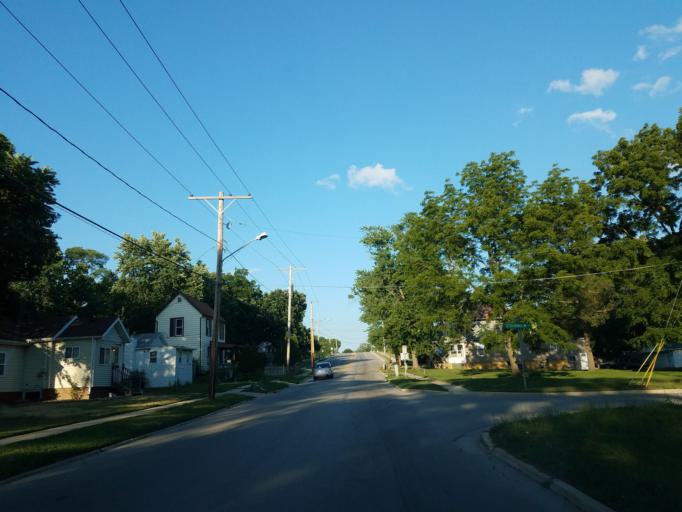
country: US
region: Illinois
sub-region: McLean County
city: Bloomington
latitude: 40.4733
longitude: -89.0152
